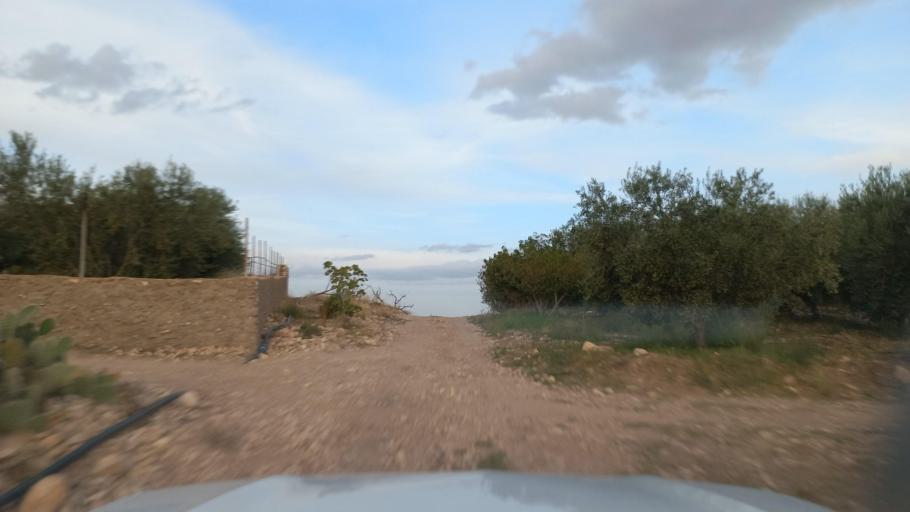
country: TN
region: Al Qasrayn
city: Sbiba
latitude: 35.4108
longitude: 9.0949
